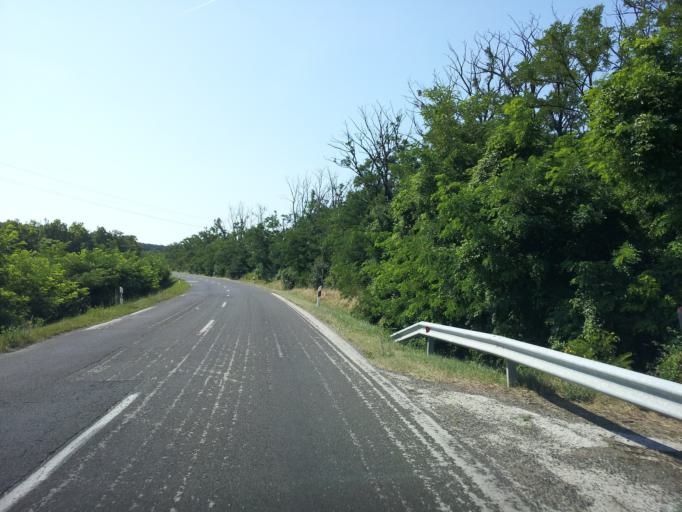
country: HU
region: Fejer
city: Lovasbereny
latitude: 47.2759
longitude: 18.5253
